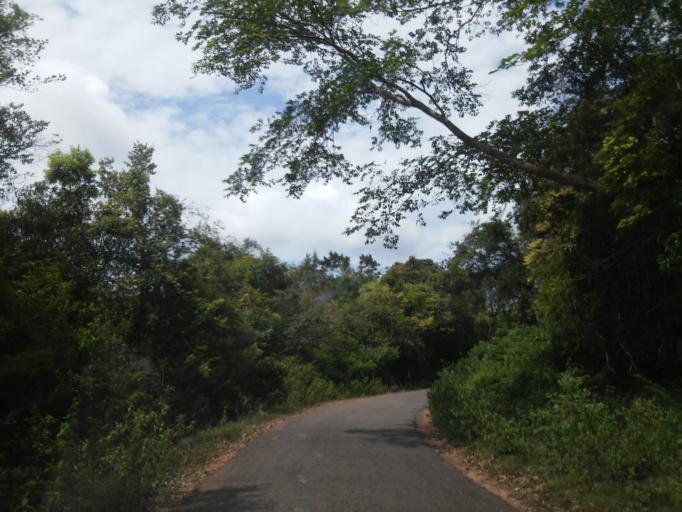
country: LK
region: Central
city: Sigiriya
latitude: 8.0894
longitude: 80.6813
